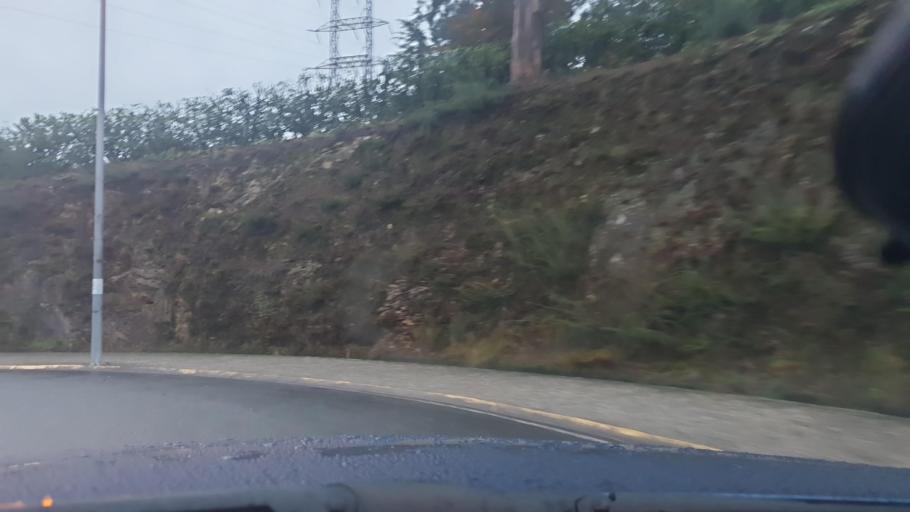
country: ES
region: Galicia
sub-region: Provincia da Coruna
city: Santiago de Compostela
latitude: 42.8522
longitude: -8.5819
